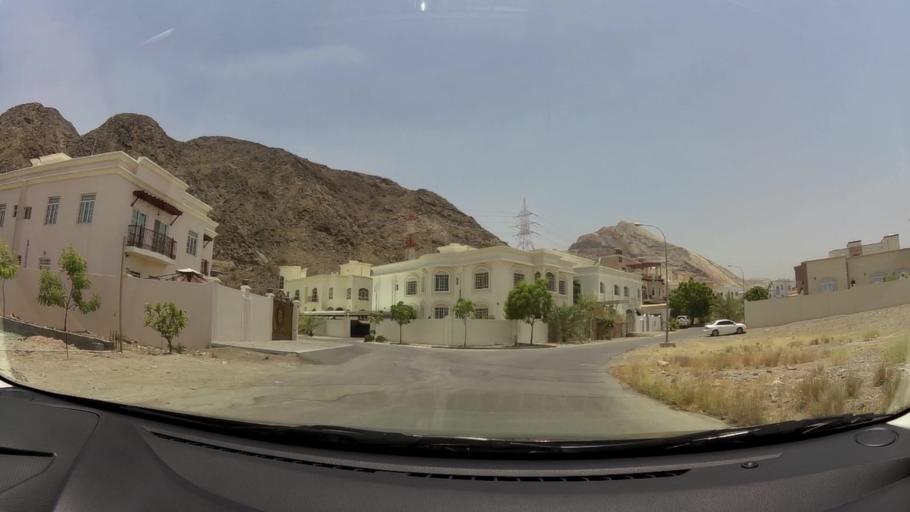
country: OM
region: Muhafazat Masqat
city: Bawshar
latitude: 23.5704
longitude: 58.4294
